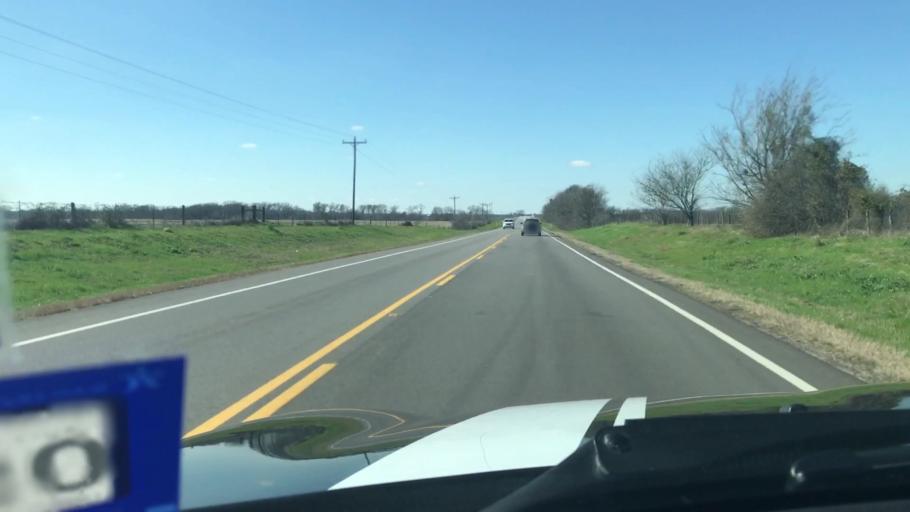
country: US
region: Texas
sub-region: Robertson County
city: Hearne
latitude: 30.8822
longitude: -96.6319
